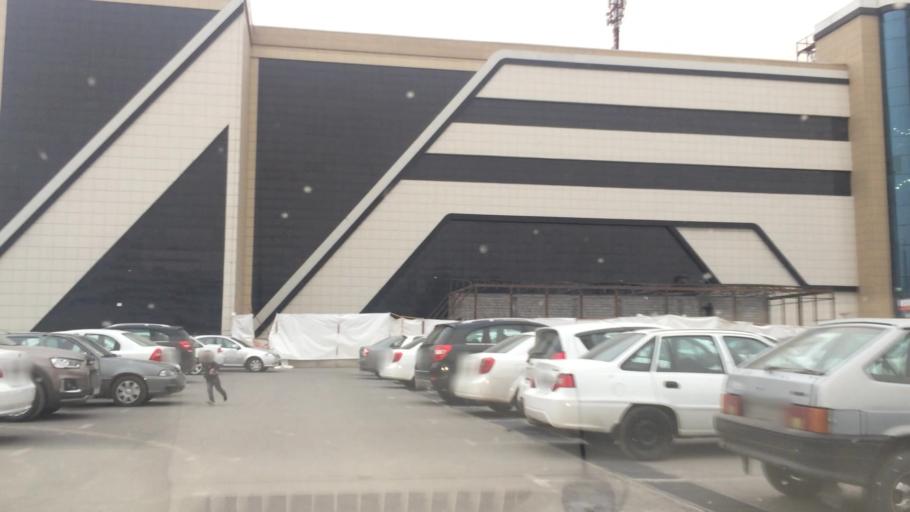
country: UZ
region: Toshkent Shahri
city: Tashkent
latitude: 41.2983
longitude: 69.2484
